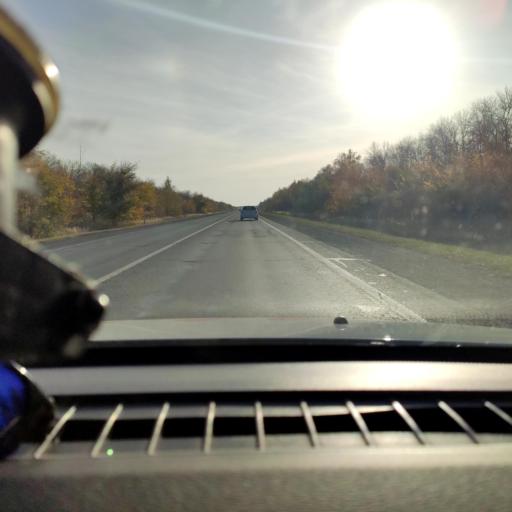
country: RU
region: Samara
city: Novokuybyshevsk
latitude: 52.9883
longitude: 49.8553
